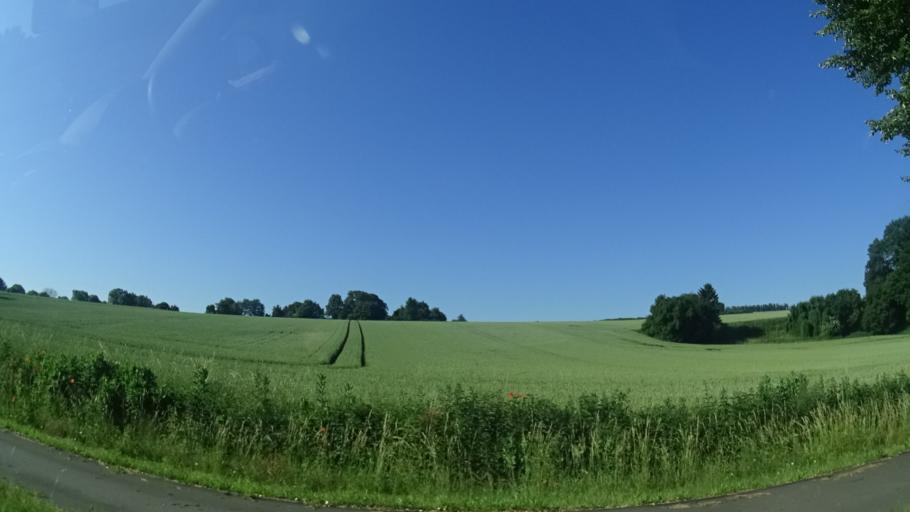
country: DE
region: Lower Saxony
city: Baddeckenstedt
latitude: 52.0856
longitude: 10.2268
